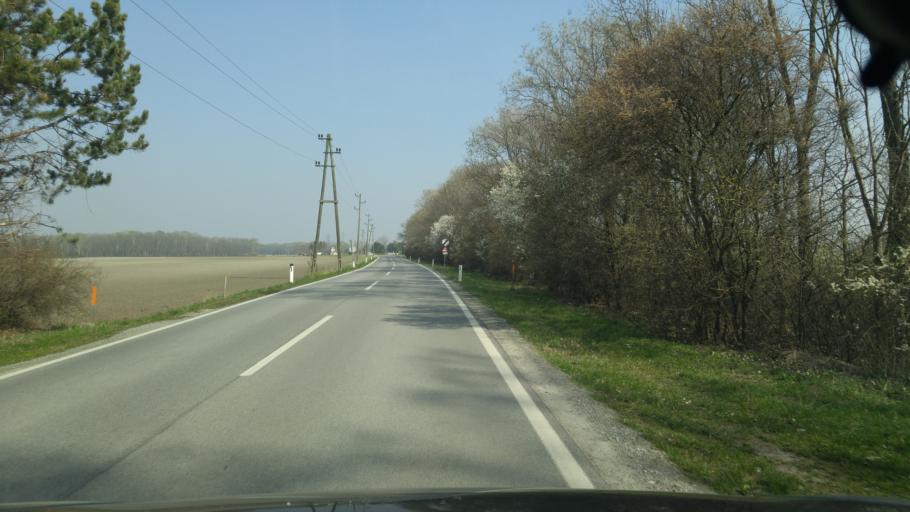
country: AT
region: Lower Austria
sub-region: Politischer Bezirk Modling
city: Munchendorf
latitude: 48.0325
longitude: 16.4148
